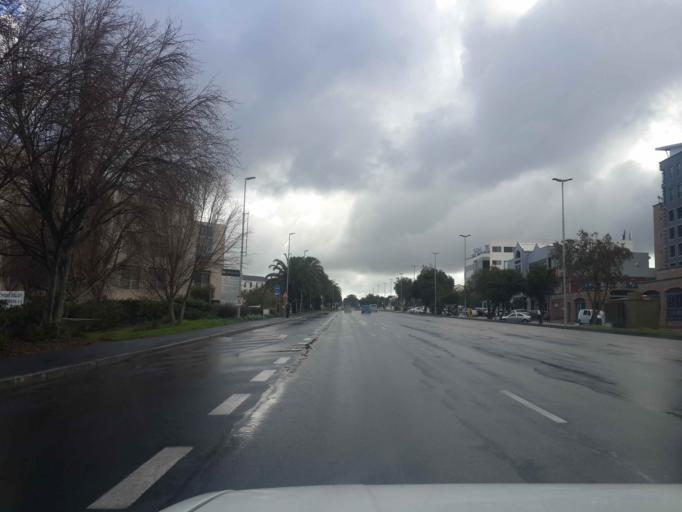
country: ZA
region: Western Cape
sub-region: City of Cape Town
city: Kraaifontein
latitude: -33.8817
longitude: 18.6351
